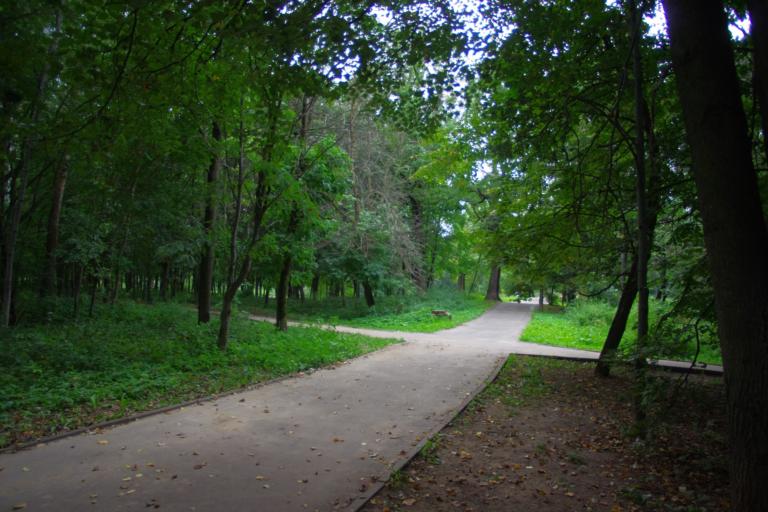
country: RU
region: Moskovskaya
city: Krasnogorsk
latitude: 55.8193
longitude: 37.3169
